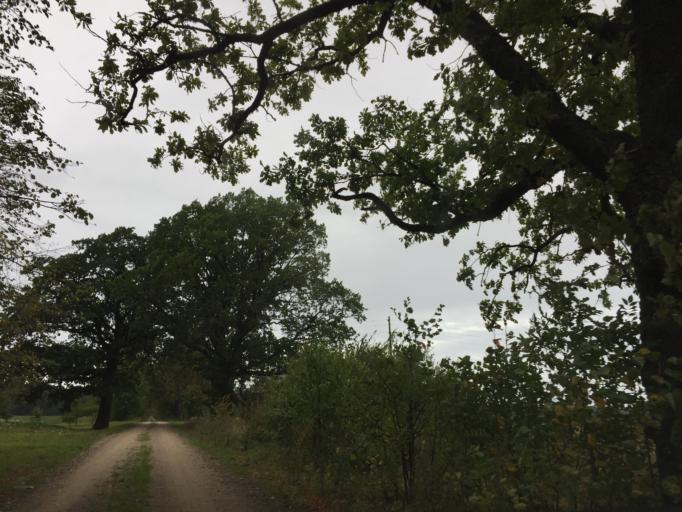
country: LV
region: Salacgrivas
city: Salacgriva
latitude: 57.7024
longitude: 24.3677
